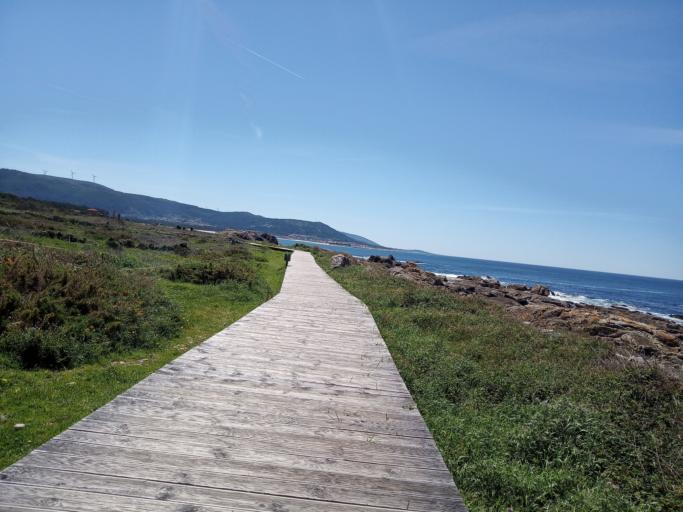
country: ES
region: Galicia
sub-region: Provincia de Pontevedra
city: A Guarda
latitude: 41.8794
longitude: -8.8798
